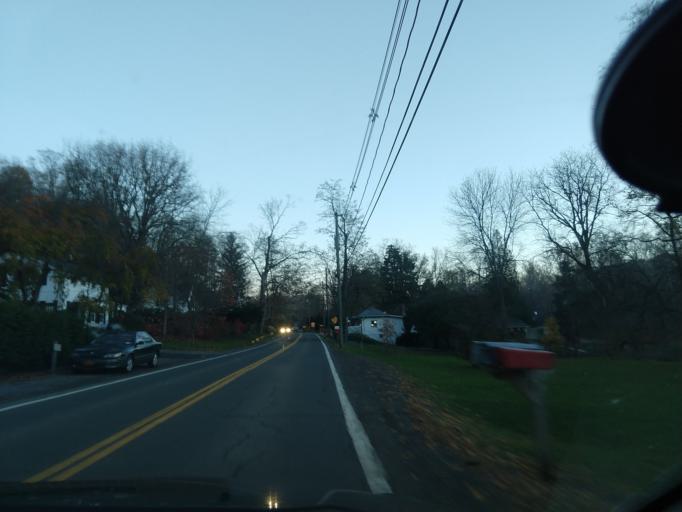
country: US
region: New York
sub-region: Tompkins County
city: East Ithaca
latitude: 42.4529
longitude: -76.4695
